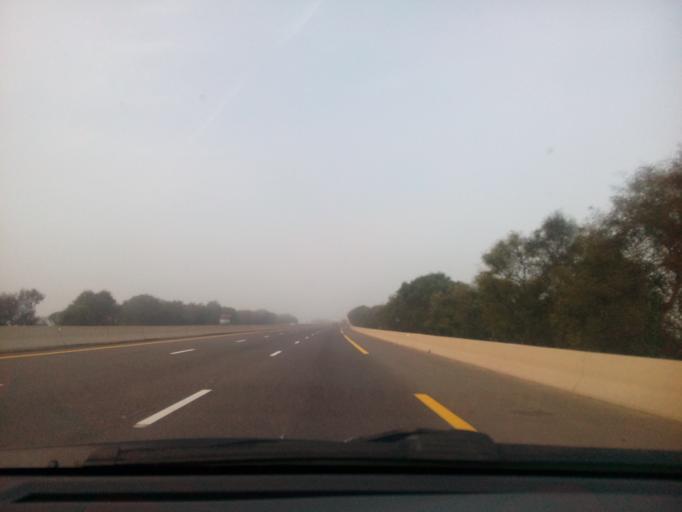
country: DZ
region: Relizane
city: Relizane
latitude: 35.7908
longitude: 0.4649
